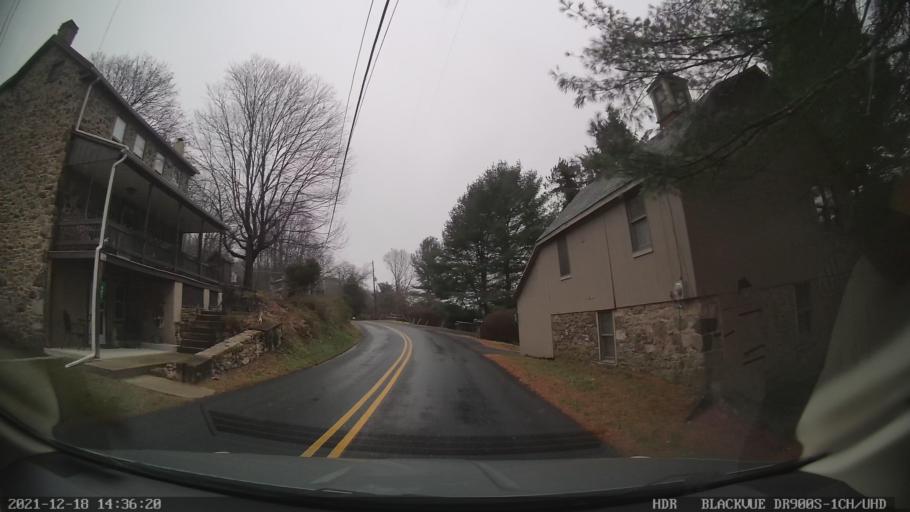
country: US
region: Pennsylvania
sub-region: Berks County
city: New Berlinville
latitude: 40.3857
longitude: -75.6516
